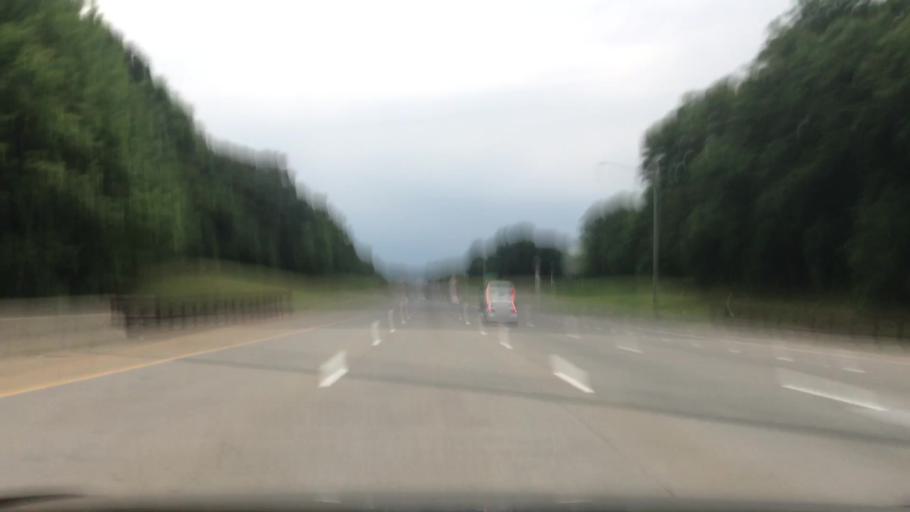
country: US
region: New Jersey
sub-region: Monmouth County
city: Shark River Hills
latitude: 40.2082
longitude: -74.0973
